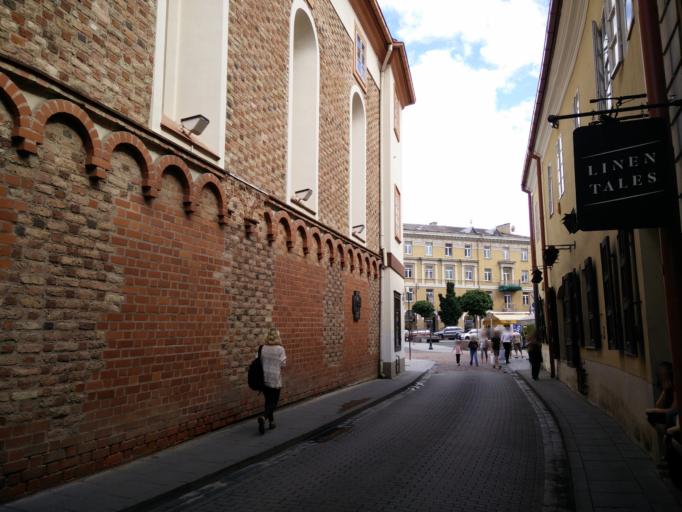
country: LT
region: Vilnius County
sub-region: Vilnius
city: Vilnius
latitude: 54.6795
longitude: 25.2869
